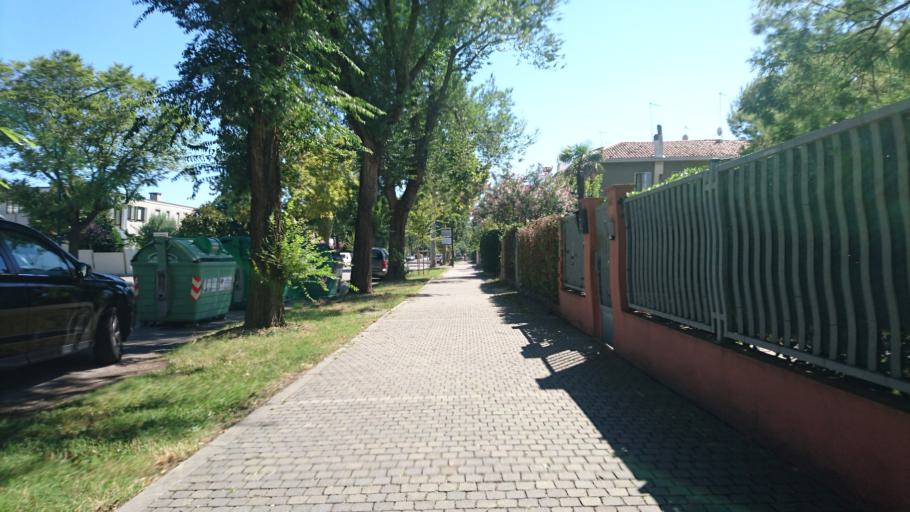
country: IT
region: Veneto
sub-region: Provincia di Venezia
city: Lido
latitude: 45.3931
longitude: 12.3543
